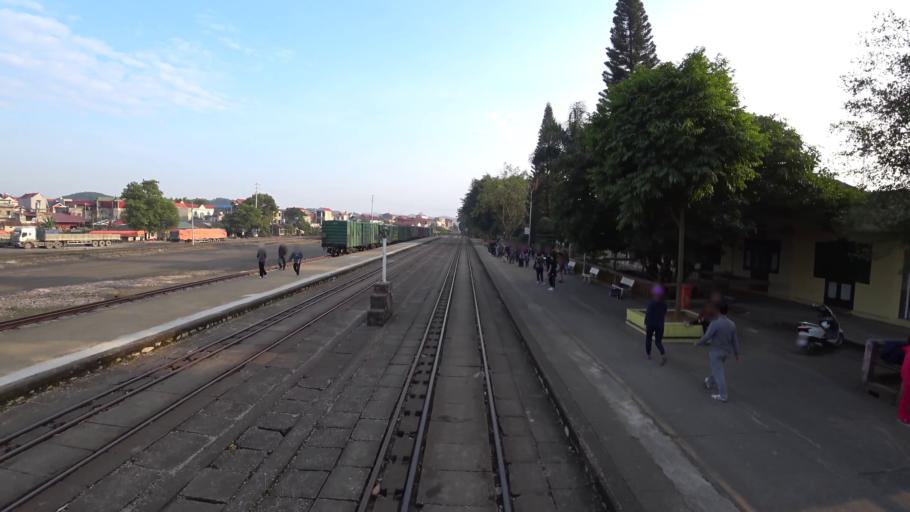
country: VN
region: Lang Son
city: Thi Tran Cao Loc
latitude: 21.8652
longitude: 106.7641
